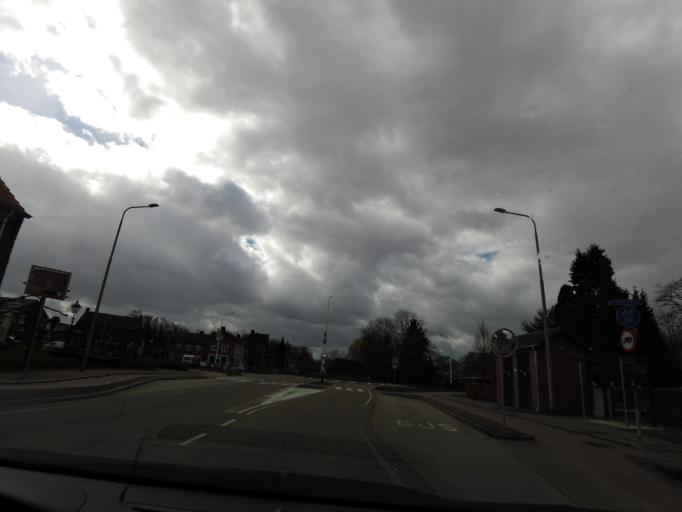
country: NL
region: Limburg
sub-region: Gemeente Beesel
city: Offenbeek
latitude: 51.3128
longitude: 6.1104
